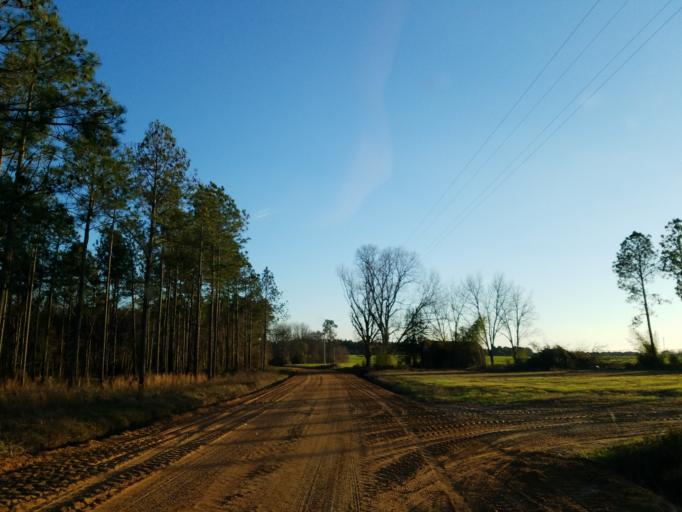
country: US
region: Georgia
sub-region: Worth County
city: Sylvester
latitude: 31.5913
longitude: -83.7882
